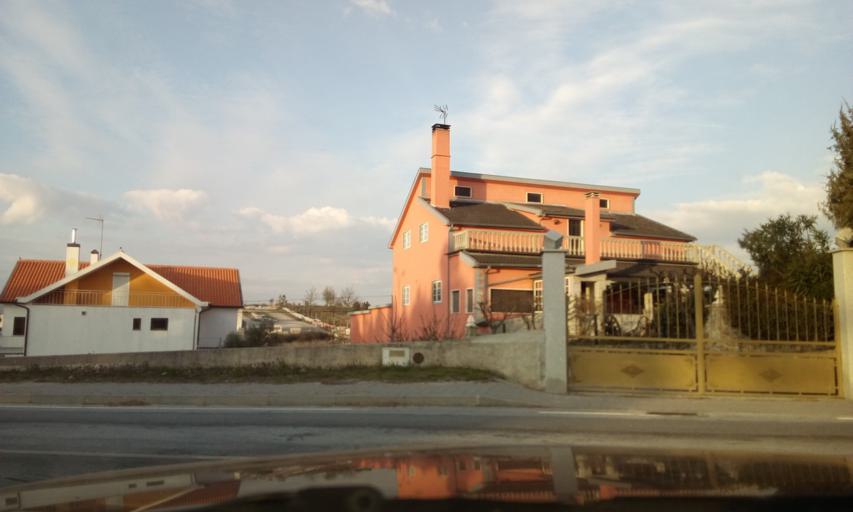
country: ES
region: Castille and Leon
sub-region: Provincia de Salamanca
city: Fuentes de Onoro
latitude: 40.5987
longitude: -6.9971
